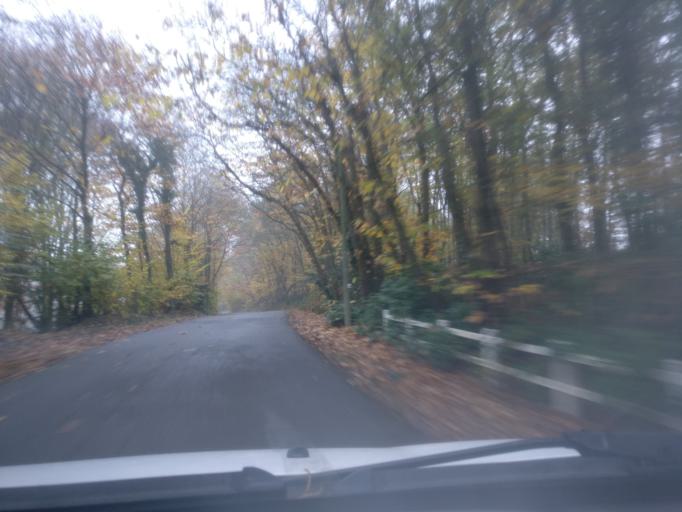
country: FR
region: Brittany
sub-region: Departement d'Ille-et-Vilaine
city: Bruz
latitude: 47.9990
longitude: -1.7450
